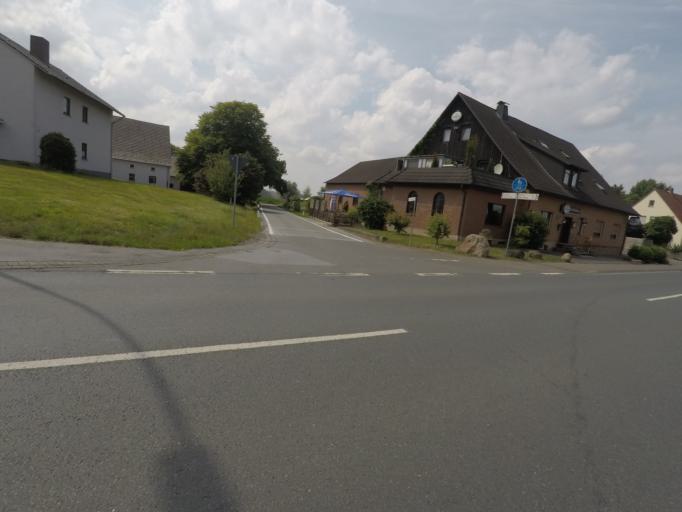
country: DE
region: North Rhine-Westphalia
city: Enger
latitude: 52.1617
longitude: 8.5661
